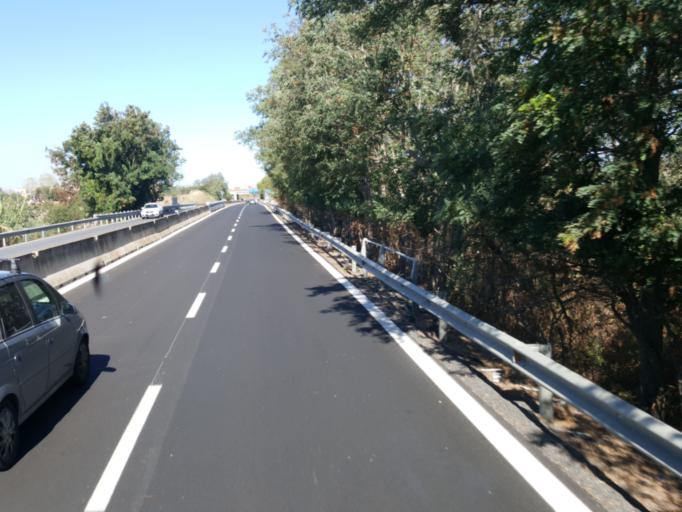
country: IT
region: Latium
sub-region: Provincia di Viterbo
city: Montalto di Castro
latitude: 42.3464
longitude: 11.6101
